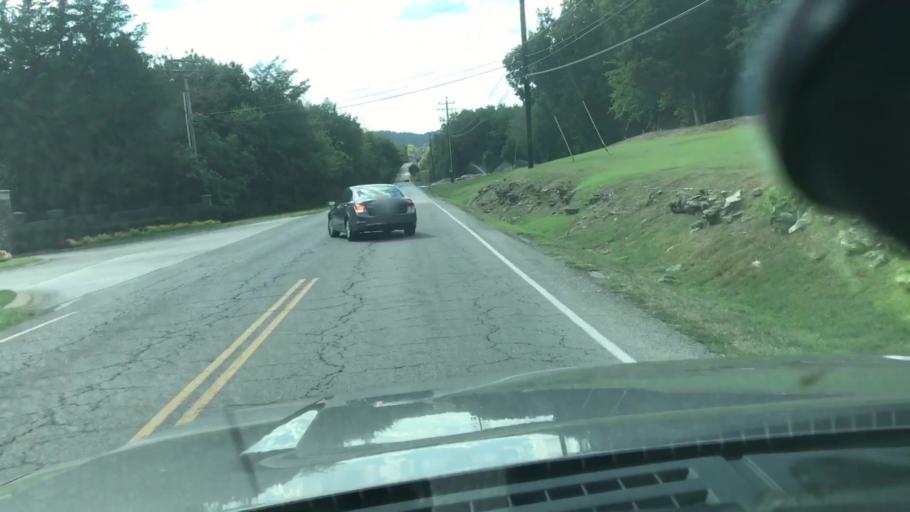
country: US
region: Tennessee
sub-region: Davidson County
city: Forest Hills
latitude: 36.0261
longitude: -86.8961
